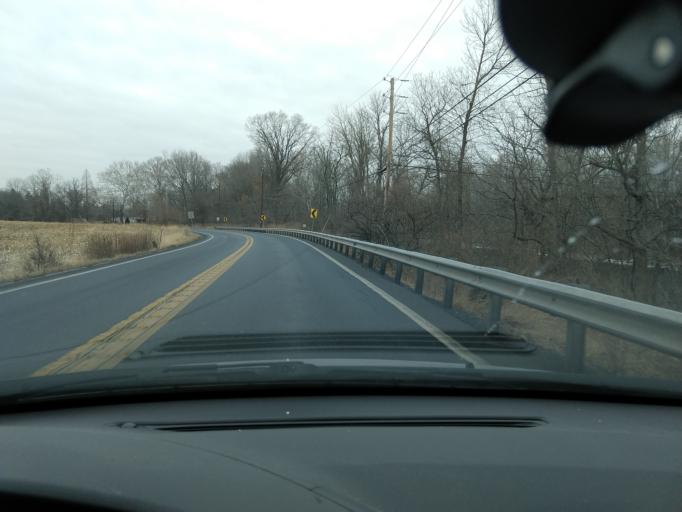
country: US
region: Pennsylvania
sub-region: Berks County
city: Amity Gardens
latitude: 40.2529
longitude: -75.7298
